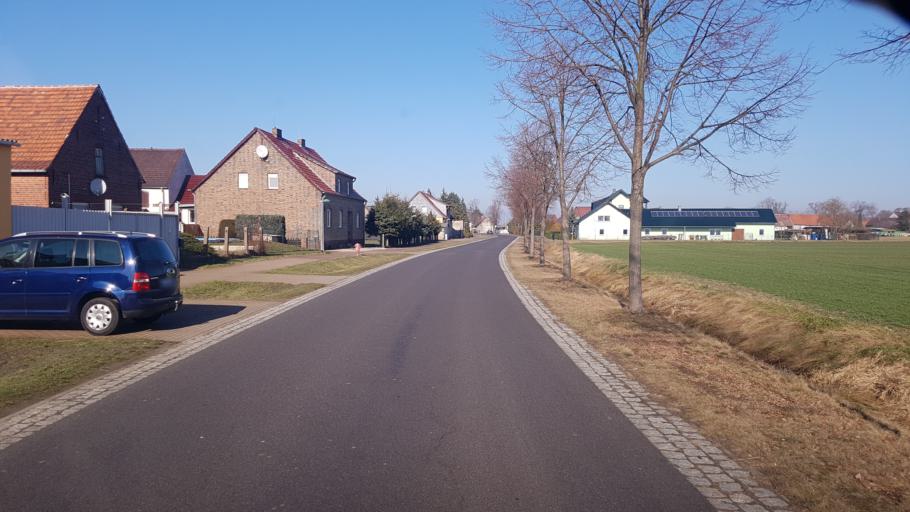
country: DE
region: Brandenburg
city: Ihlow
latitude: 51.8208
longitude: 13.3488
